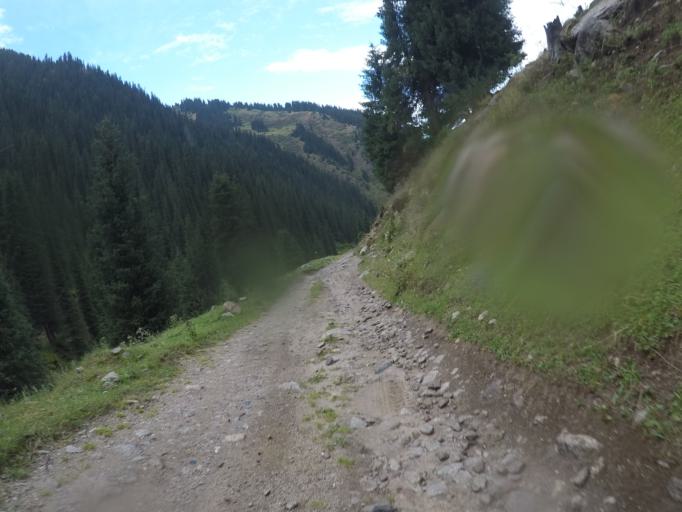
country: KG
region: Ysyk-Koel
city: Teploklyuchenka
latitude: 42.4114
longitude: 78.5762
